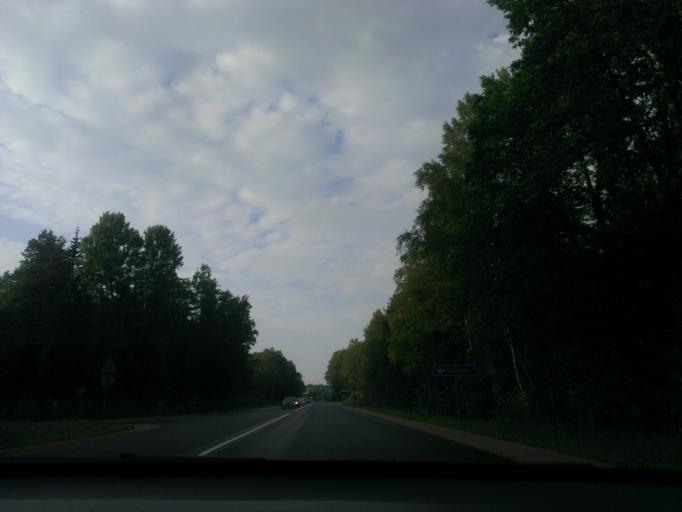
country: LV
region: Kekava
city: Kekava
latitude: 56.7091
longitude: 24.2466
